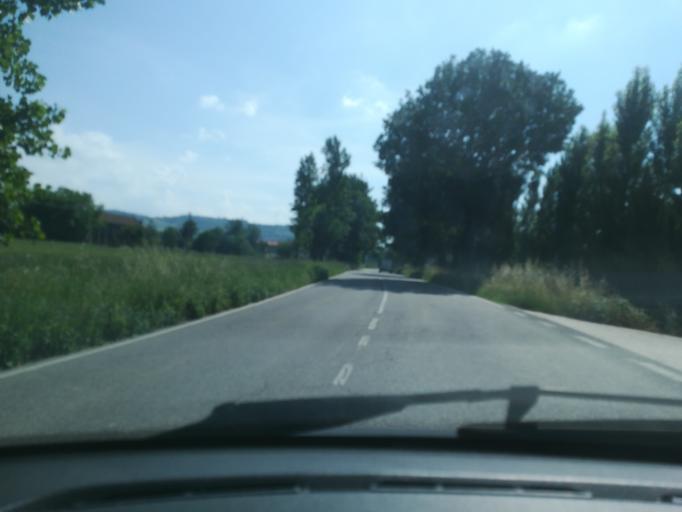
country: IT
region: The Marches
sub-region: Provincia di Macerata
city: Pollenza
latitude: 43.2936
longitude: 13.3703
